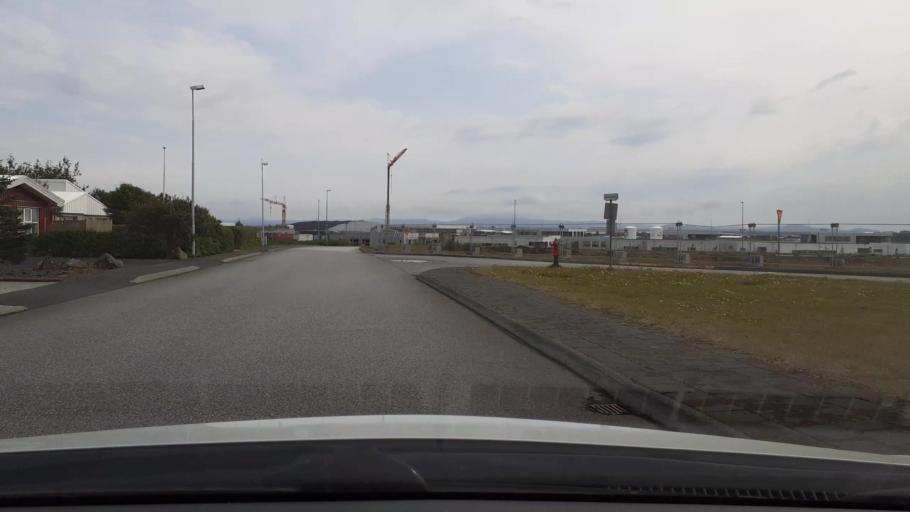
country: IS
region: Southern Peninsula
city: Reykjanesbaer
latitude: 63.9962
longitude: -22.5705
